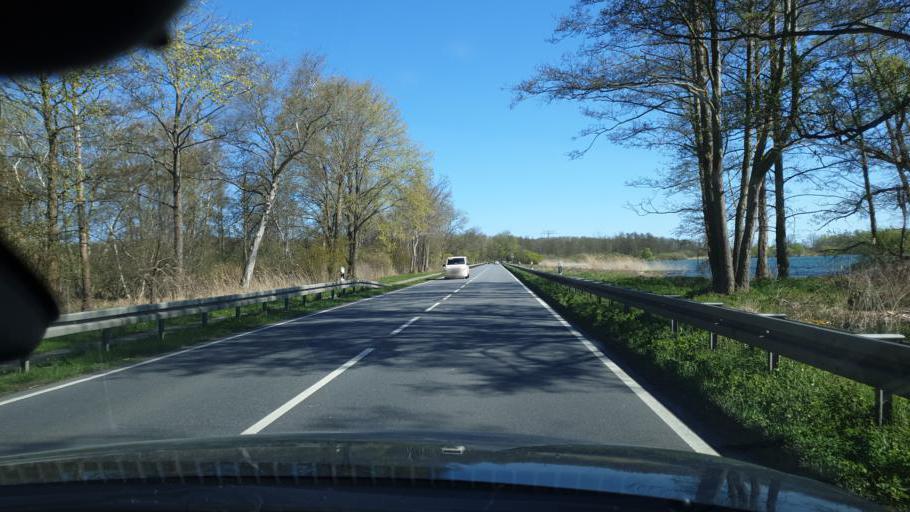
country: DE
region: Mecklenburg-Vorpommern
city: Seehof
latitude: 53.6806
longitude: 11.4625
